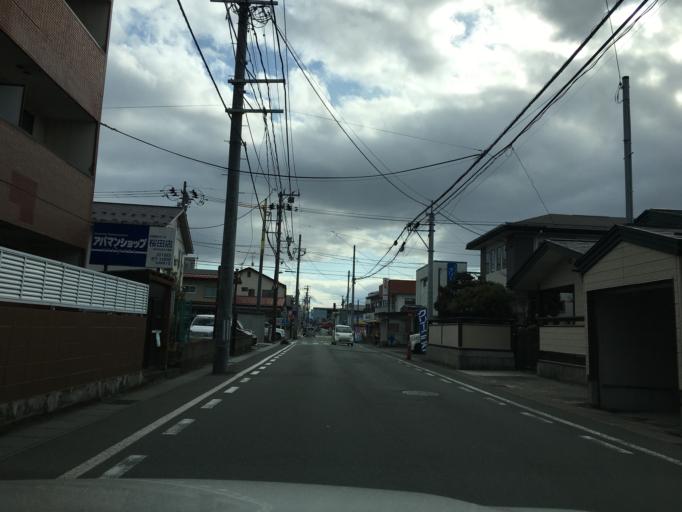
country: JP
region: Yamagata
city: Yamagata-shi
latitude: 38.2538
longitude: 140.3228
